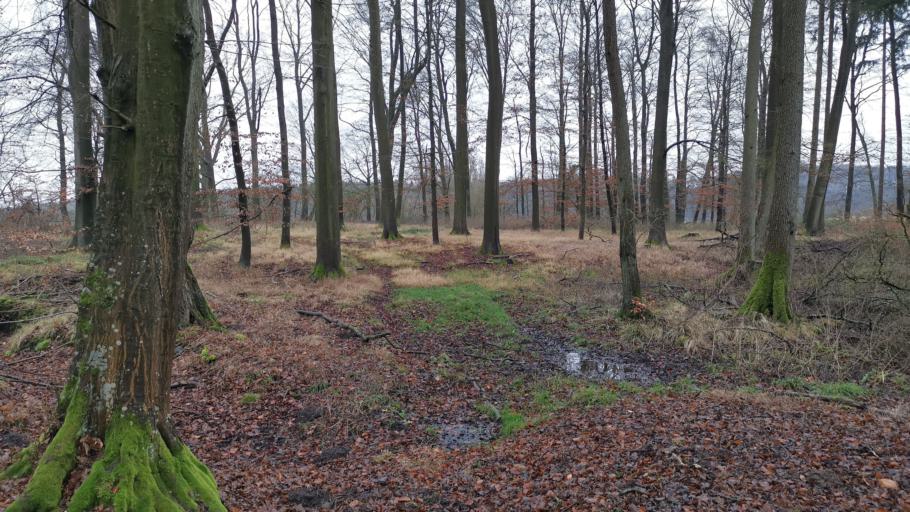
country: DE
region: Schleswig-Holstein
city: Lehmrade
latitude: 53.6024
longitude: 10.7834
